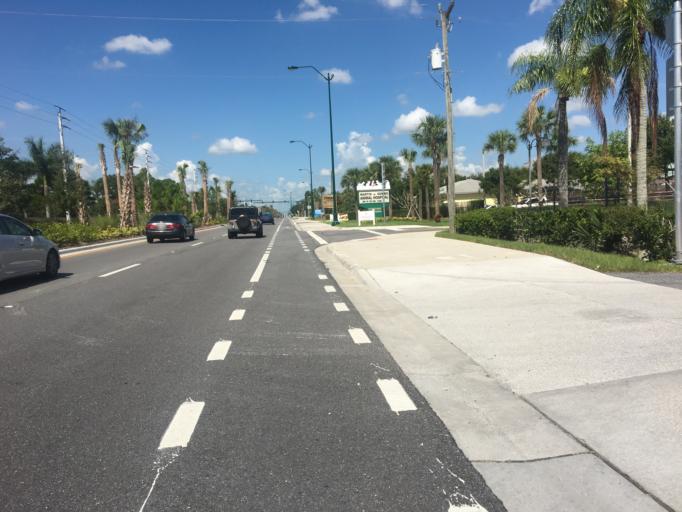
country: US
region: Florida
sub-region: Martin County
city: Palm City
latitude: 27.1612
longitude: -80.2743
